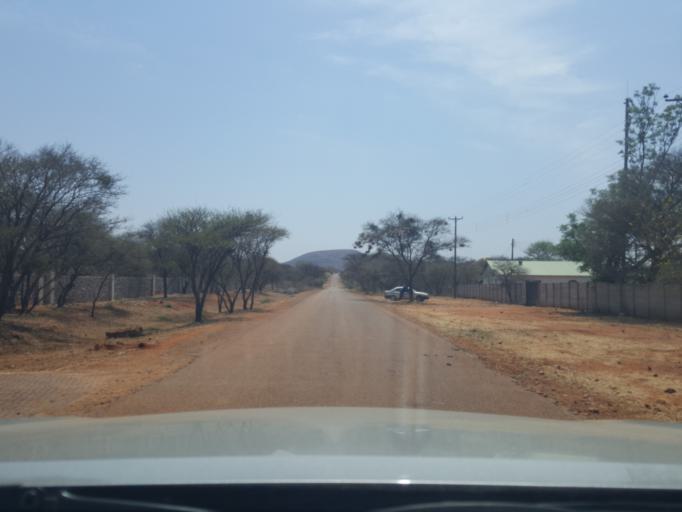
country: BW
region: South East
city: Ramotswa
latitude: -24.7721
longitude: 25.8452
